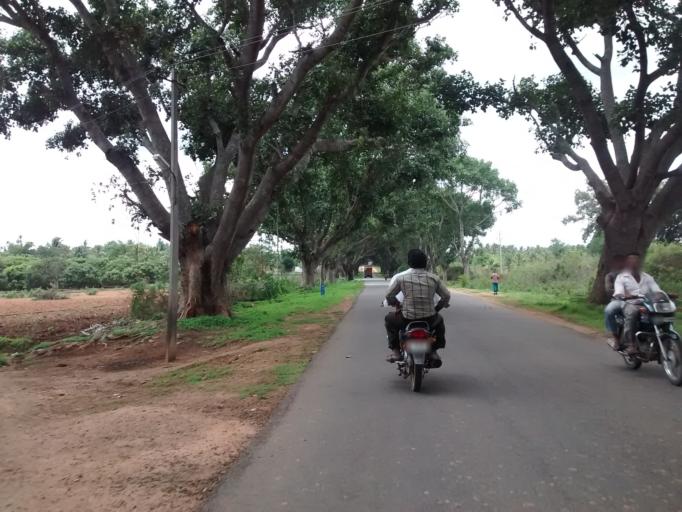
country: IN
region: Karnataka
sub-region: Tumkur
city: Kunigal
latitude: 13.1202
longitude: 77.1554
